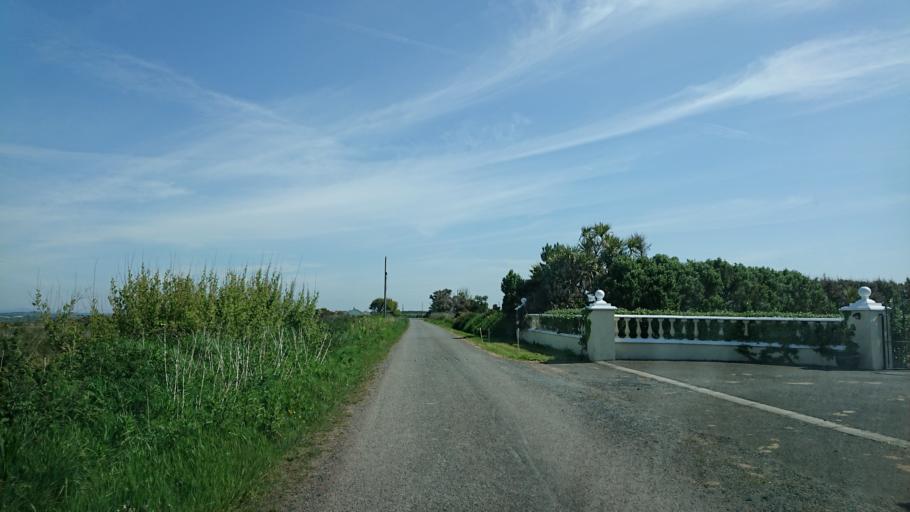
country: IE
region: Munster
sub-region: Waterford
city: Tra Mhor
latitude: 52.1372
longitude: -7.0926
